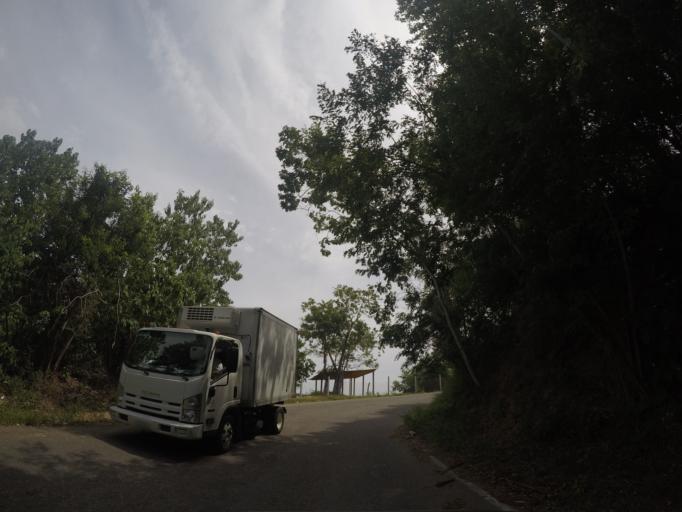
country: MX
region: Oaxaca
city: Santa Maria Tonameca
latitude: 15.6680
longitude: -96.5319
